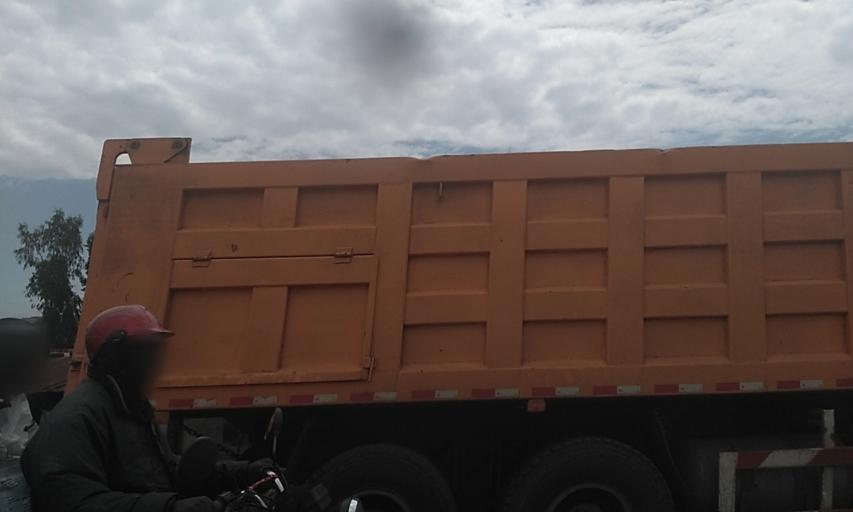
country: UG
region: Central Region
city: Kampala Central Division
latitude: 0.3489
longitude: 32.5594
